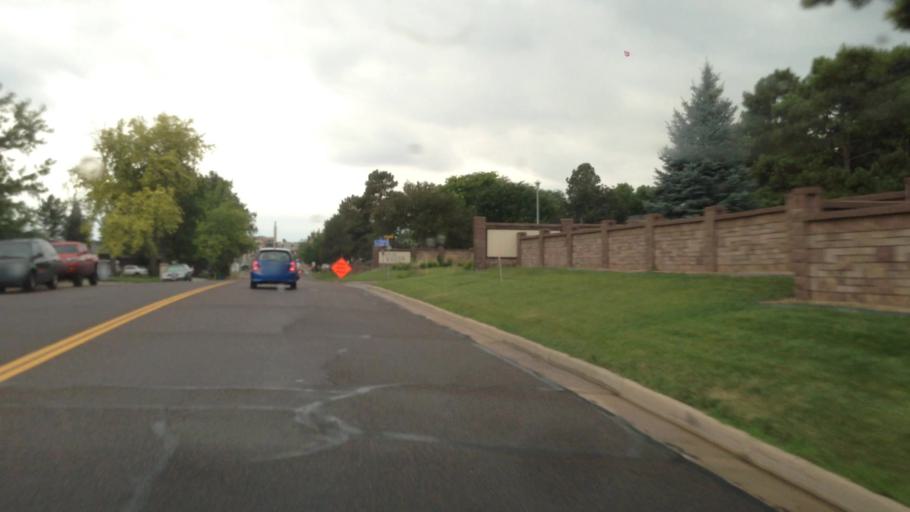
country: US
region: Colorado
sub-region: Jefferson County
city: Lakewood
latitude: 39.7147
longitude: -105.0769
